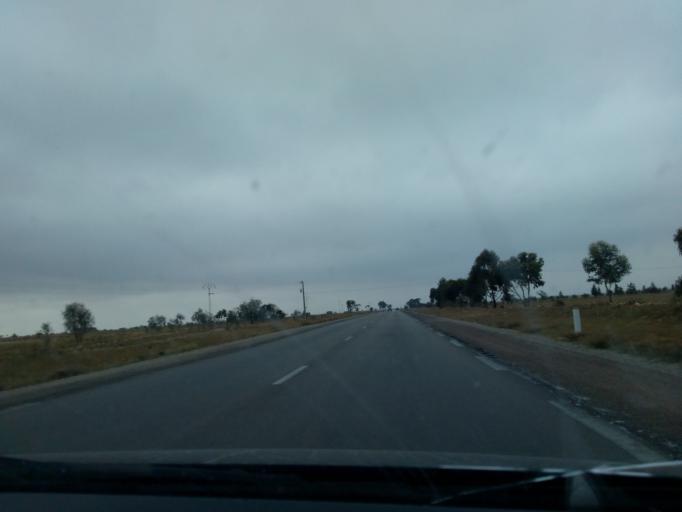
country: TN
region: Madanin
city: Medenine
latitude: 33.2778
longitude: 10.4691
